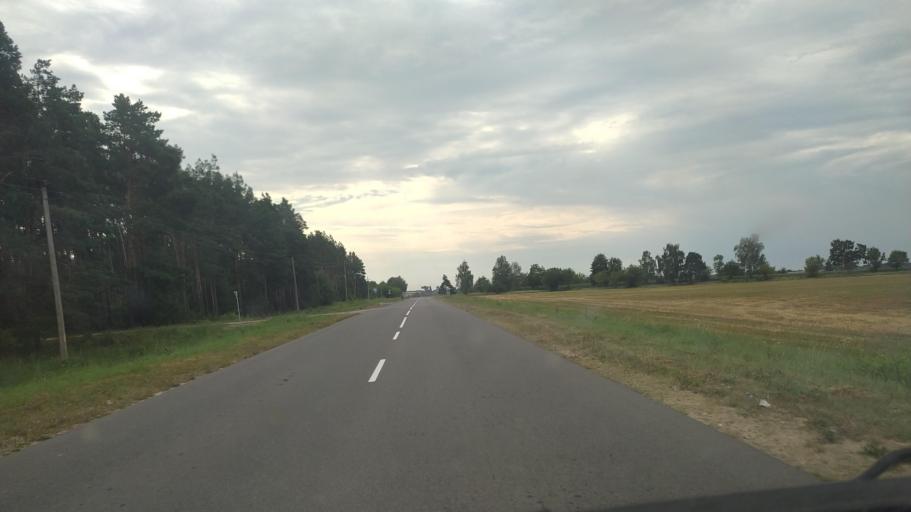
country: BY
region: Brest
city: Byaroza
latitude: 52.5594
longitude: 24.9115
